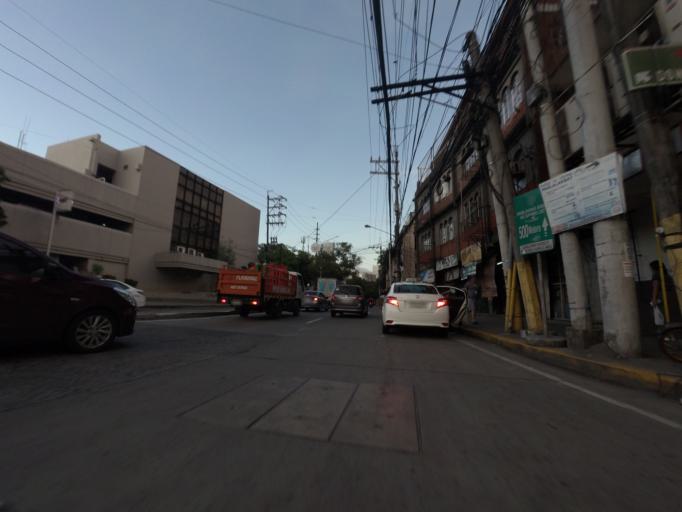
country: PH
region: Metro Manila
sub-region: City of Manila
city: Quiapo
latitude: 14.5967
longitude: 120.9897
